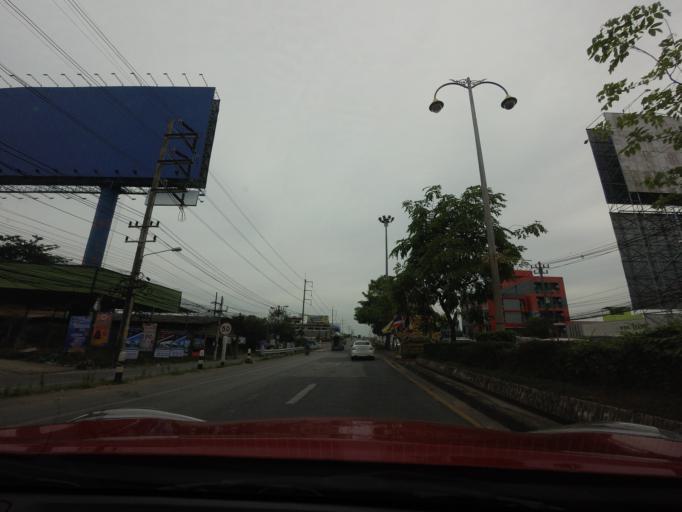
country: TH
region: Songkhla
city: Hat Yai
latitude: 6.9899
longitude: 100.4823
